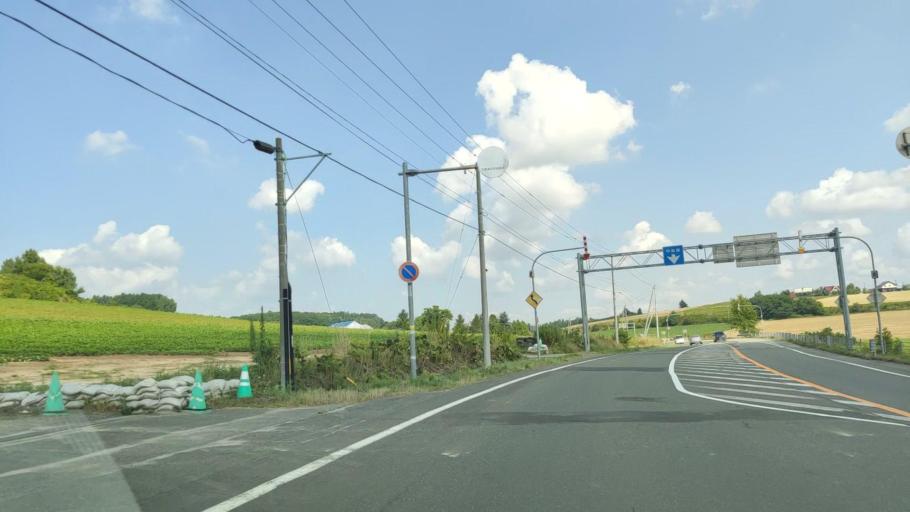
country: JP
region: Hokkaido
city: Shimo-furano
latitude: 43.5338
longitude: 142.4406
